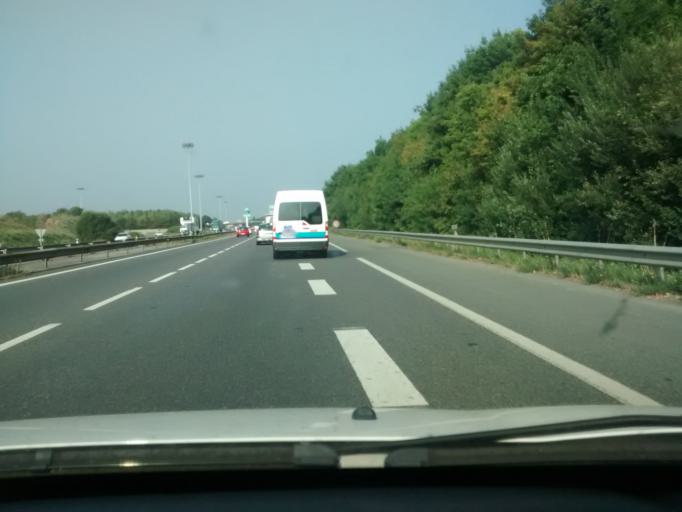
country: FR
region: Brittany
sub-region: Departement d'Ille-et-Vilaine
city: Rennes
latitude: 48.0812
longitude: -1.6680
